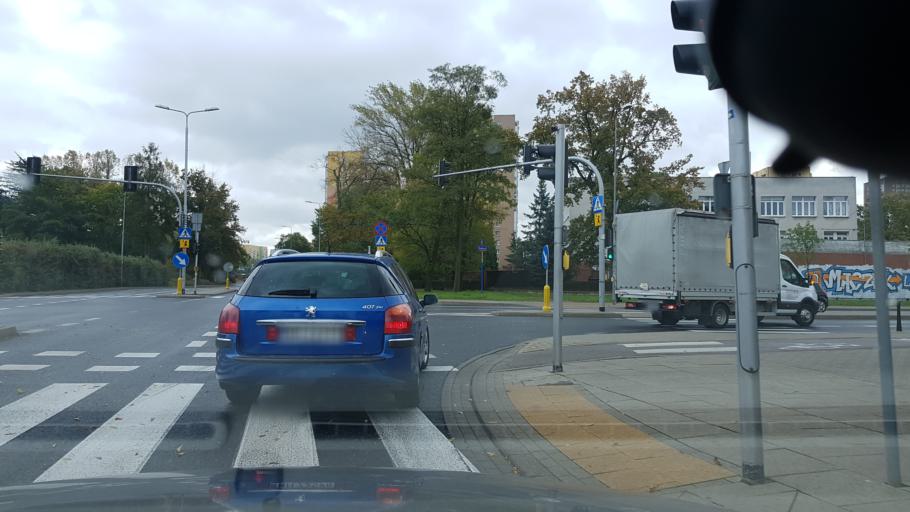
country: PL
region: Masovian Voivodeship
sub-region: Warszawa
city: Zoliborz
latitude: 52.2875
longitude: 20.9767
